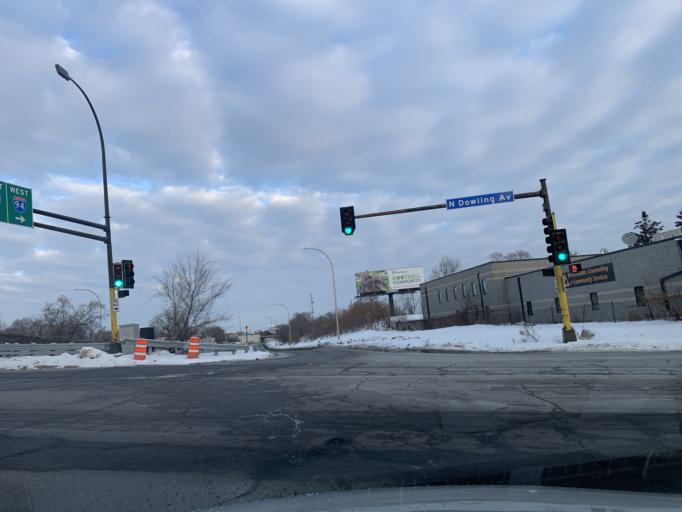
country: US
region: Minnesota
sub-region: Anoka County
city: Columbia Heights
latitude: 45.0239
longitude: -93.2838
